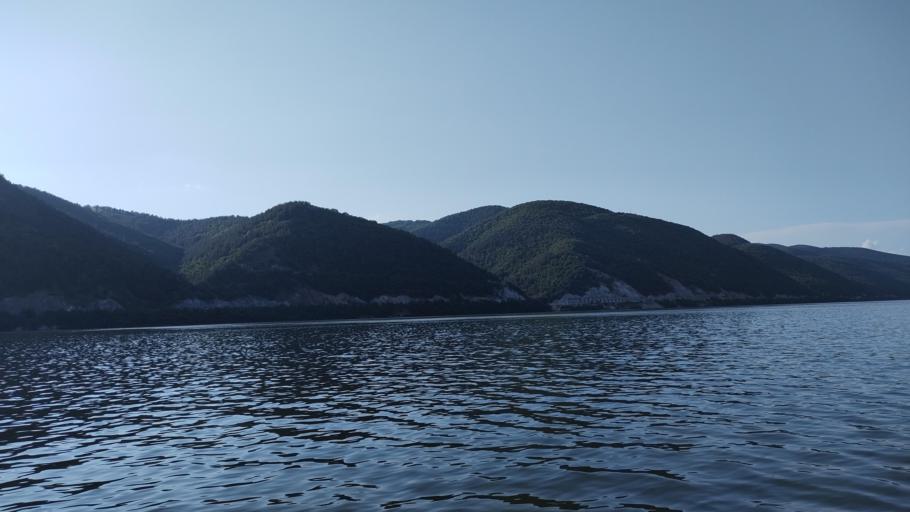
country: RO
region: Mehedinti
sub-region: Comuna Dubova
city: Dubova
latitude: 44.5340
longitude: 22.2147
